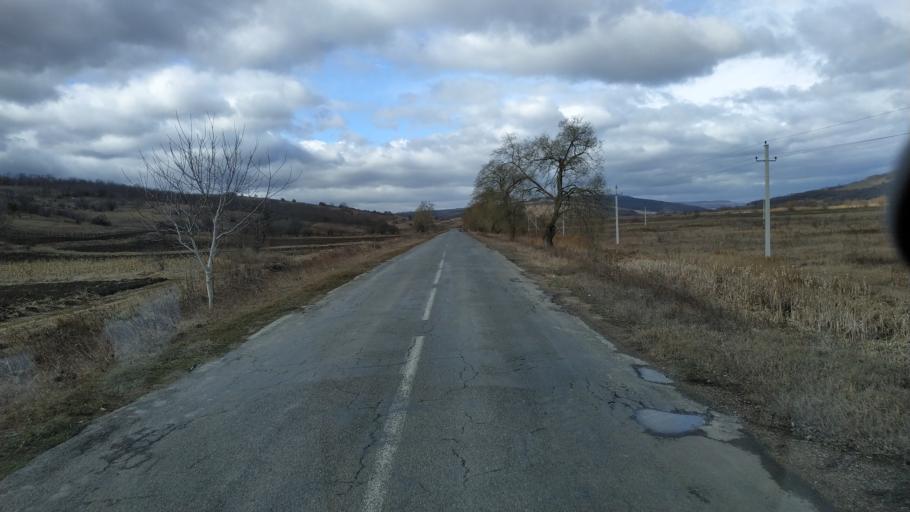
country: MD
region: Stinga Nistrului
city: Bucovat
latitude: 47.1424
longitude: 28.3741
